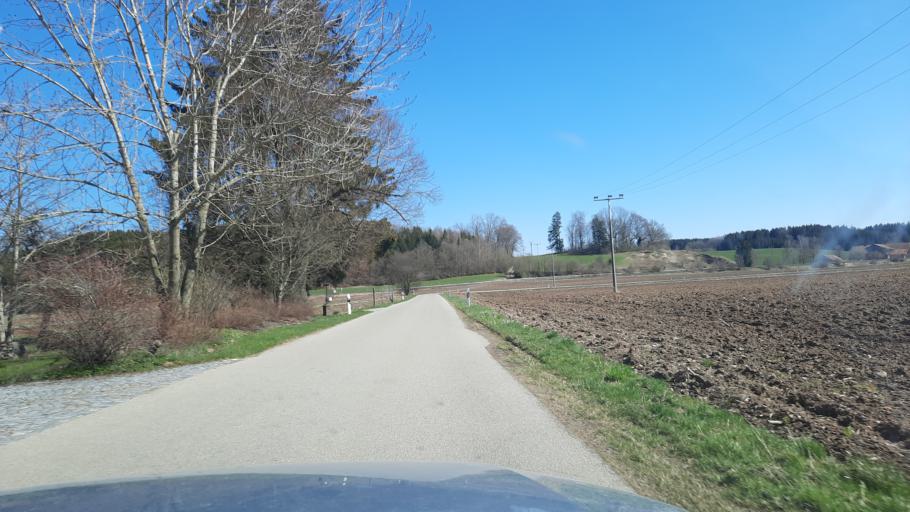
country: DE
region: Bavaria
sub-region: Swabia
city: Wolfertschwenden
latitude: 47.8543
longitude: 10.2520
